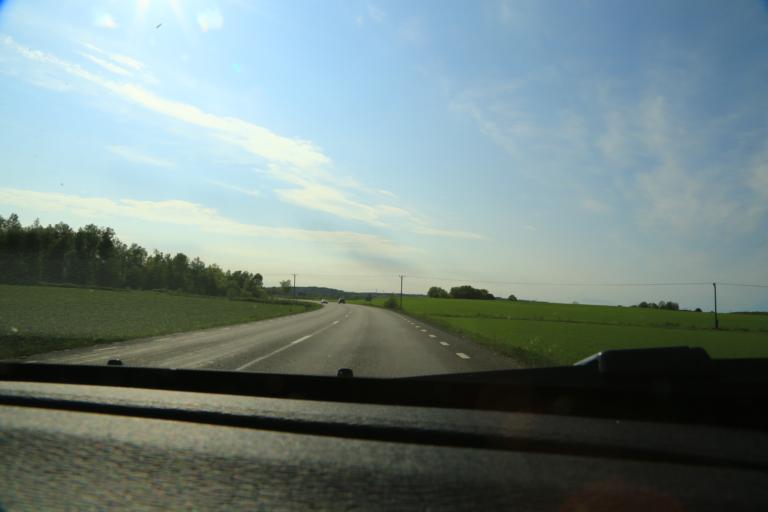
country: SE
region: Halland
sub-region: Kungsbacka Kommun
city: Frillesas
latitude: 57.2458
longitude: 12.2091
